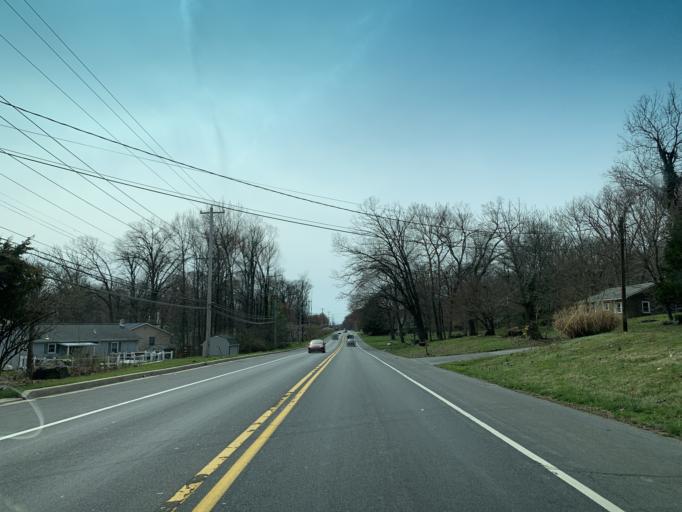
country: US
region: Delaware
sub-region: New Castle County
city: Glasgow
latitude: 39.6331
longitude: -75.7502
